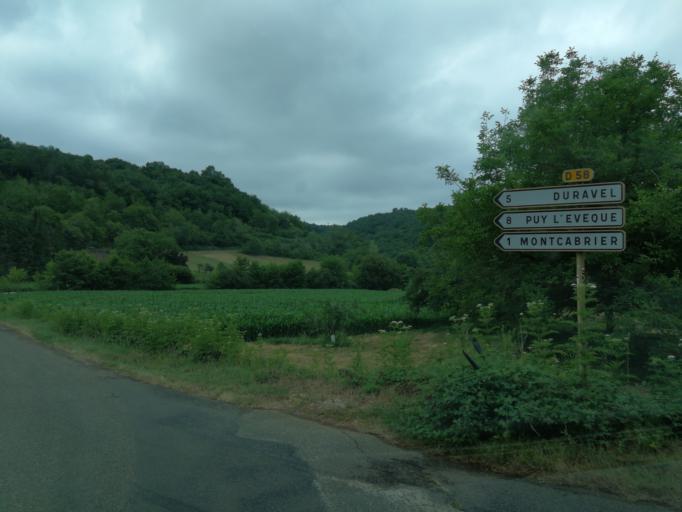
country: FR
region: Aquitaine
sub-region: Departement du Lot-et-Garonne
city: Montayral
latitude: 44.5445
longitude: 1.0699
